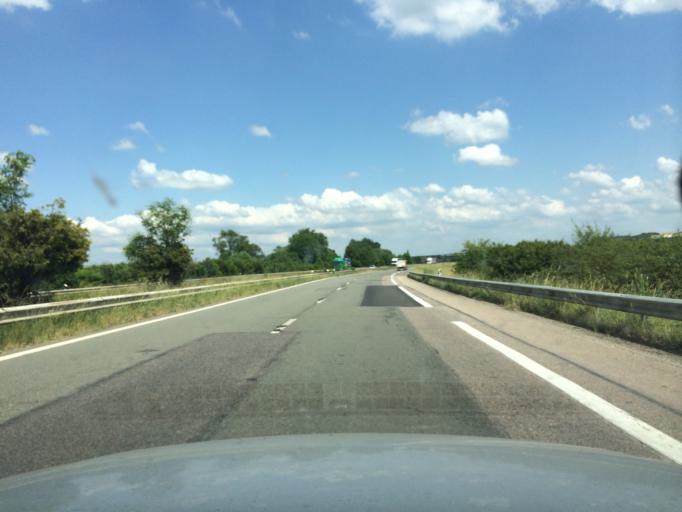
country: FR
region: Lorraine
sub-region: Departement de Meurthe-et-Moselle
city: Foug
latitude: 48.6899
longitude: 5.6978
